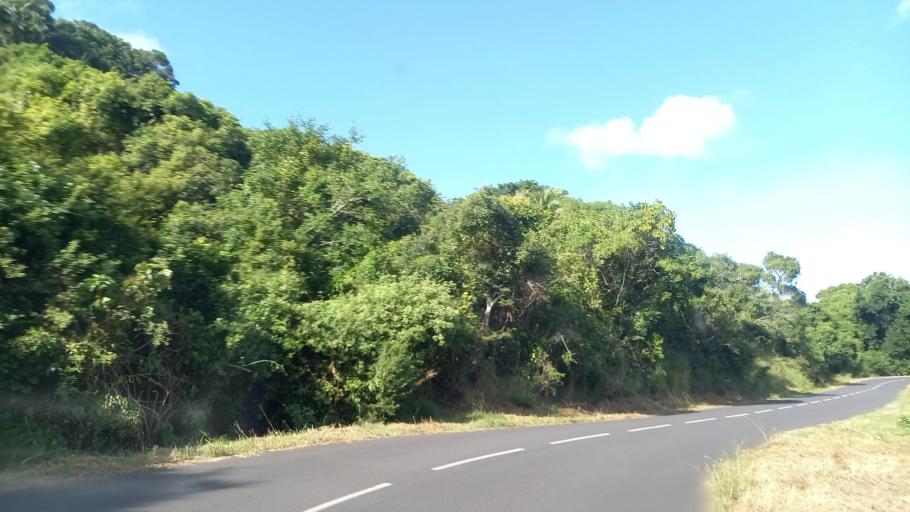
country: YT
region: Kani-Keli
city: Kani Keli
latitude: -12.9718
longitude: 45.1110
